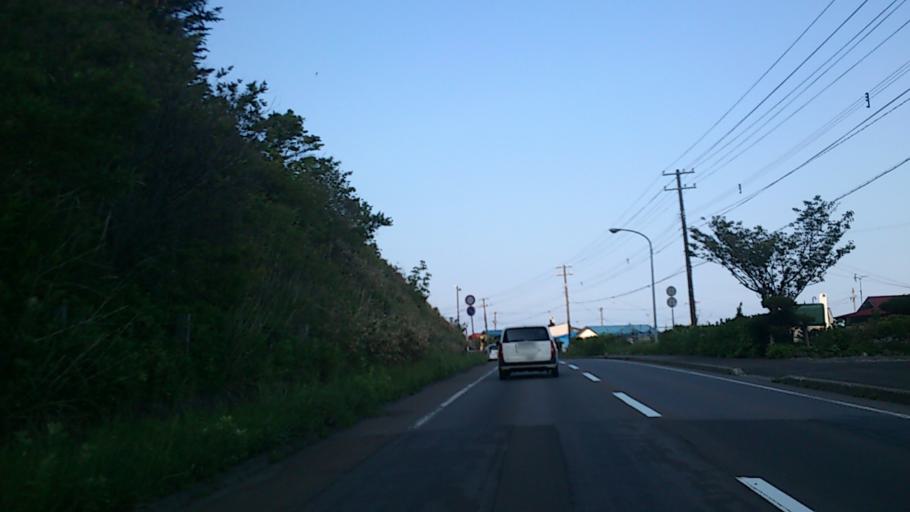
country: JP
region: Hokkaido
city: Kamiiso
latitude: 41.4654
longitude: 140.2535
